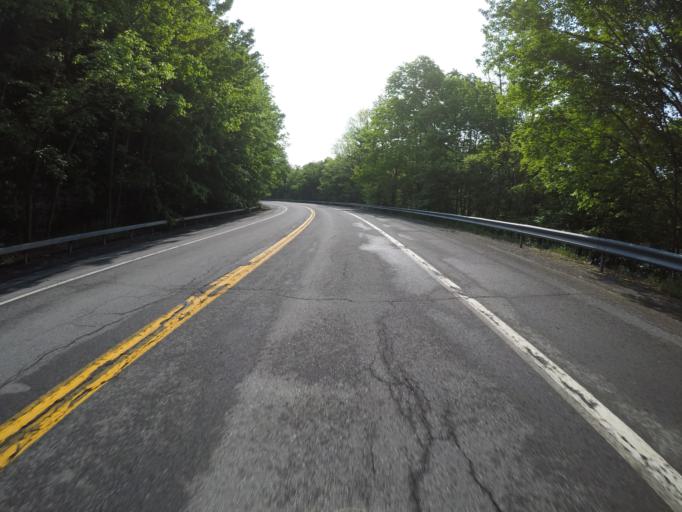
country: US
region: New York
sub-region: Sullivan County
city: Livingston Manor
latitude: 42.0888
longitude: -74.8015
